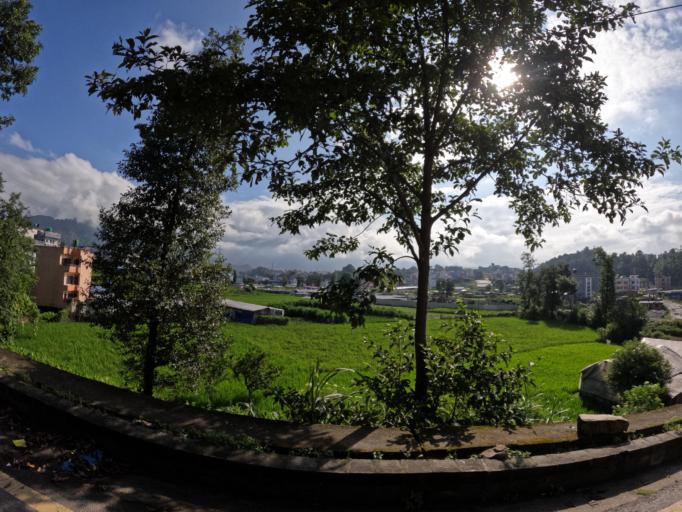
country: NP
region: Central Region
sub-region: Bagmati Zone
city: Kathmandu
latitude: 27.7596
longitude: 85.3339
